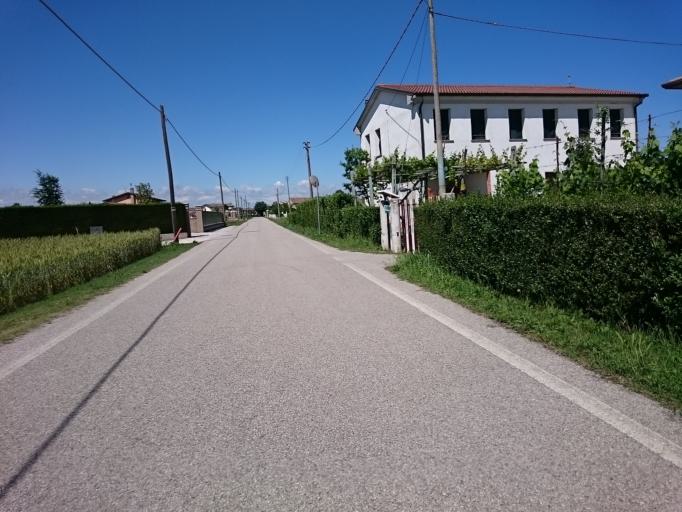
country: IT
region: Veneto
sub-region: Provincia di Padova
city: Codevigo
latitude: 45.2504
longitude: 12.0988
